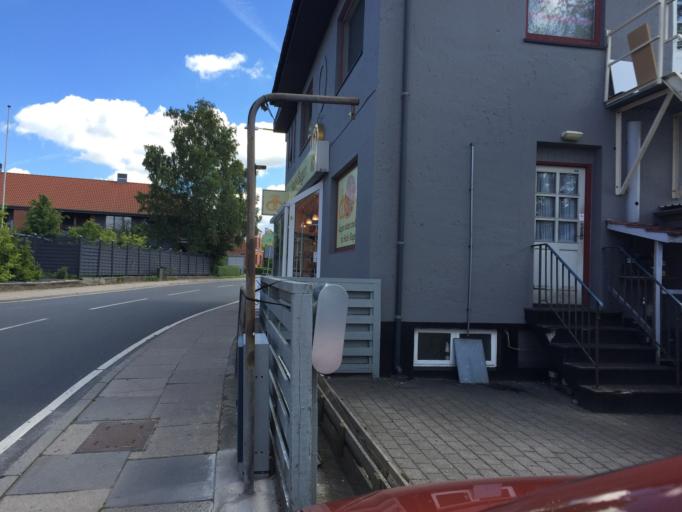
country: DK
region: South Denmark
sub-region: Kerteminde Kommune
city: Langeskov
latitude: 55.3589
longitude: 10.5908
